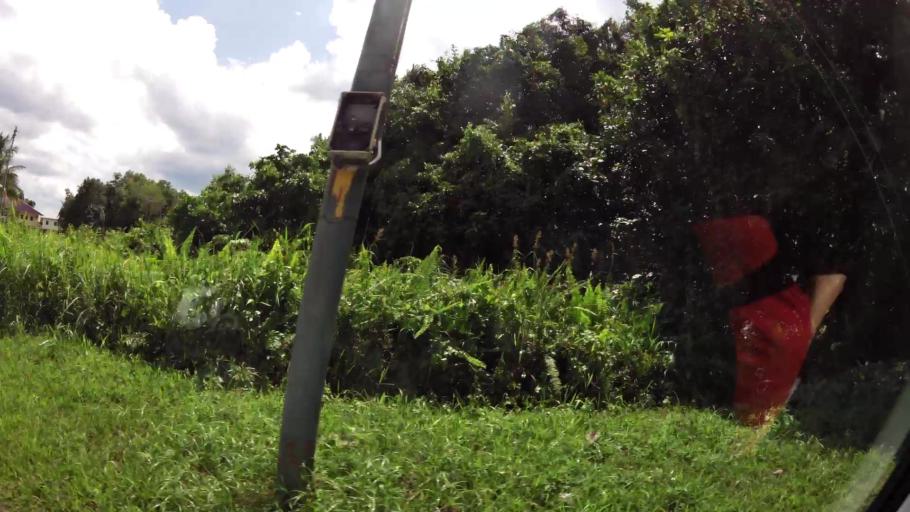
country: BN
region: Brunei and Muara
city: Bandar Seri Begawan
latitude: 4.9466
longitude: 114.9595
